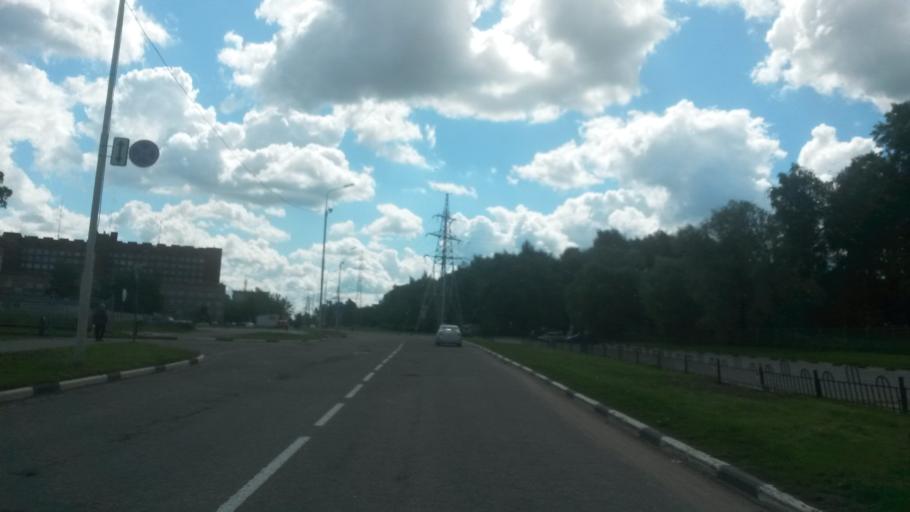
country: RU
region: Jaroslavl
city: Yaroslavl
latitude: 57.5877
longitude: 39.8485
